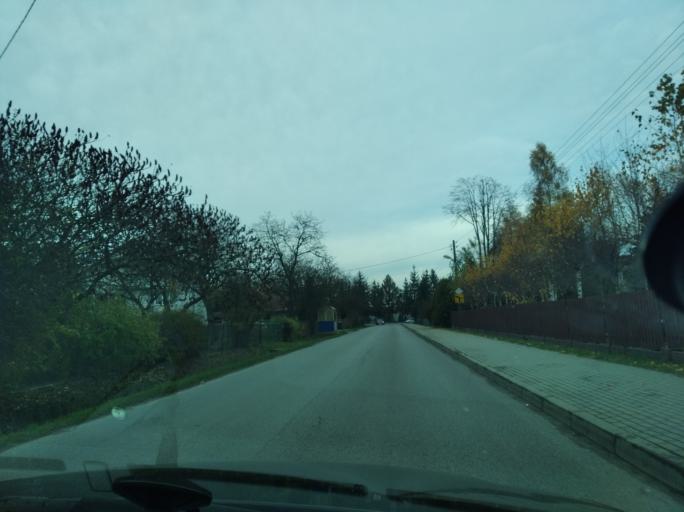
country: PL
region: Subcarpathian Voivodeship
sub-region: Powiat przeworski
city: Grzeska
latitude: 50.0821
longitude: 22.4540
